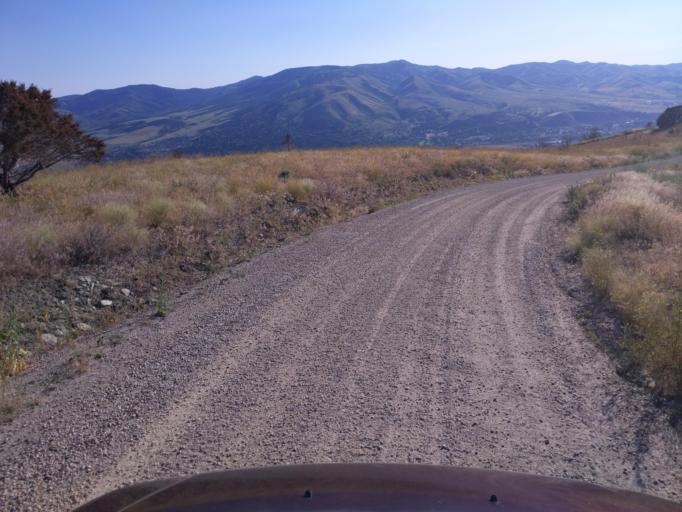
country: US
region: Idaho
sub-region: Bannock County
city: Pocatello
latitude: 42.8501
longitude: -112.3739
